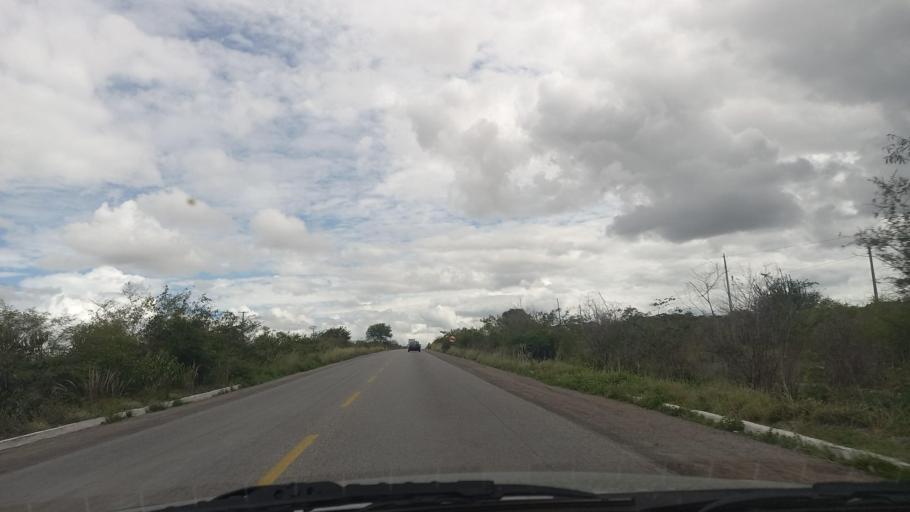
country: BR
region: Pernambuco
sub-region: Cachoeirinha
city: Cachoeirinha
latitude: -8.3428
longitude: -36.1624
